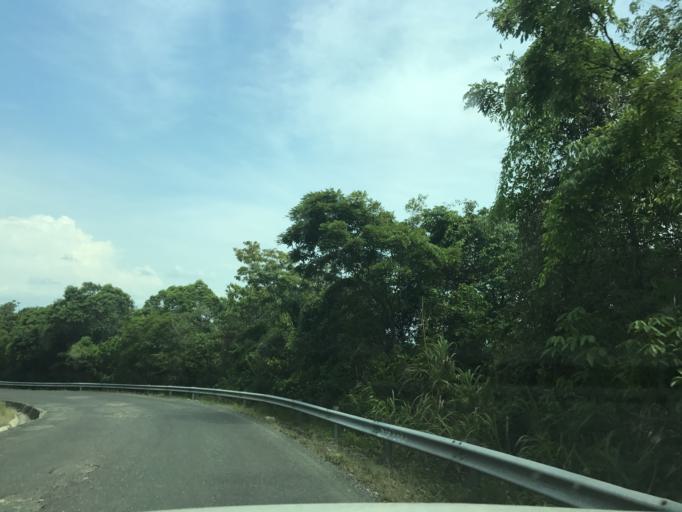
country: GT
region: Izabal
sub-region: Municipio de Los Amates
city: Los Amates
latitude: 15.3858
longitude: -89.0247
